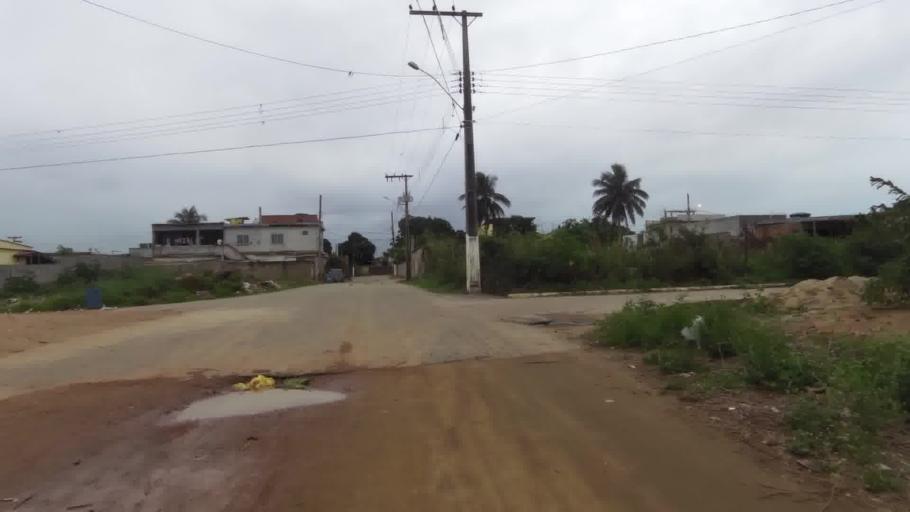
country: BR
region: Espirito Santo
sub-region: Marataizes
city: Marataizes
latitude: -21.0489
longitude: -40.8355
